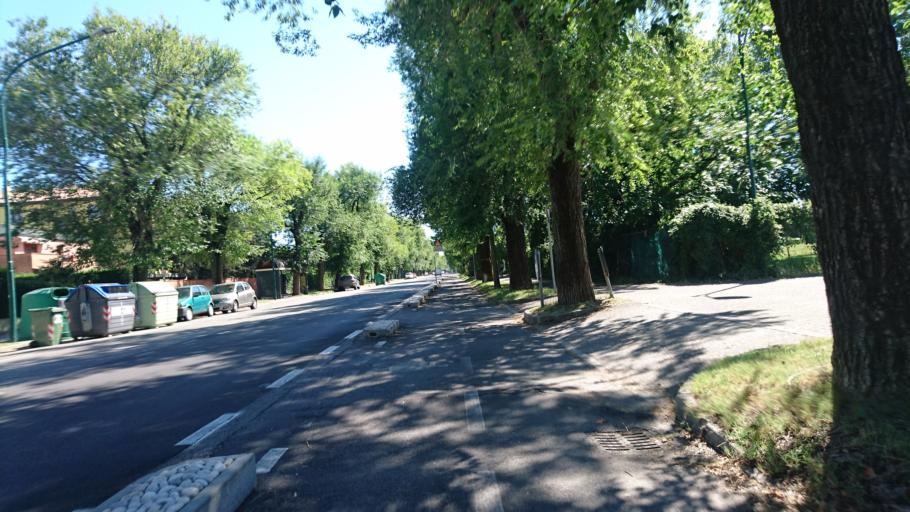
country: IT
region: Veneto
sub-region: Provincia di Venezia
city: Lido
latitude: 45.3864
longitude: 12.3491
